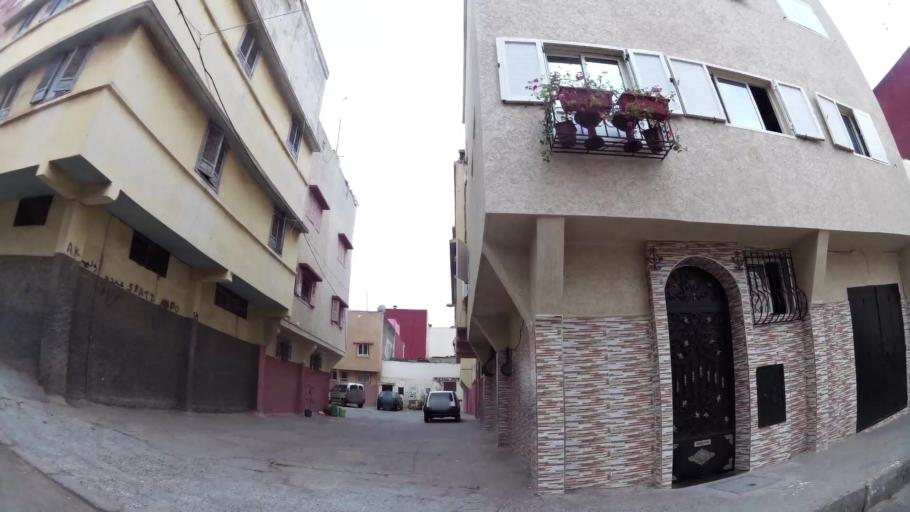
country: MA
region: Rabat-Sale-Zemmour-Zaer
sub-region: Rabat
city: Rabat
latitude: 33.9923
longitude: -6.8691
